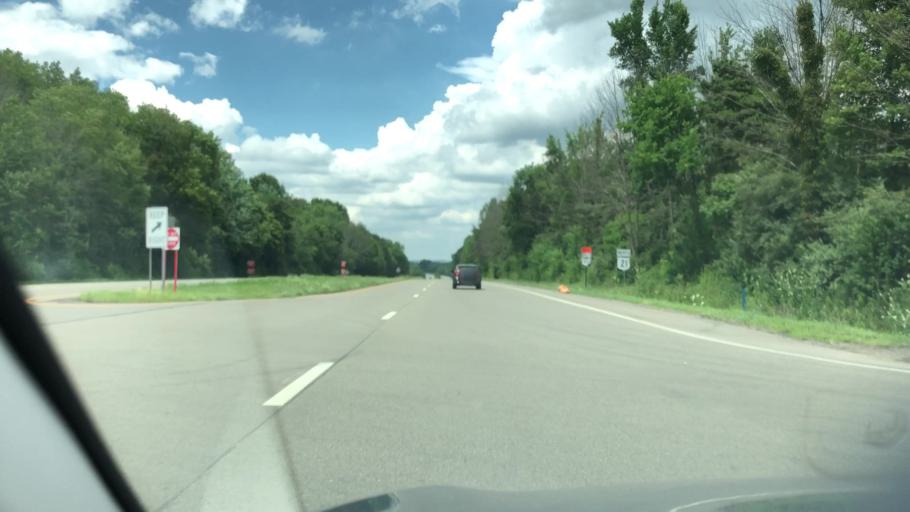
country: US
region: Ohio
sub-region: Stark County
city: Massillon
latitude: 40.8373
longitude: -81.5506
